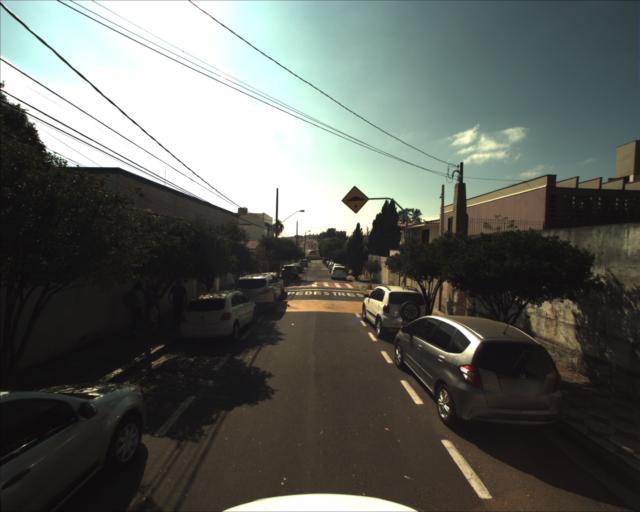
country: BR
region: Sao Paulo
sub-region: Sorocaba
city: Sorocaba
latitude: -23.4847
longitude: -47.4445
